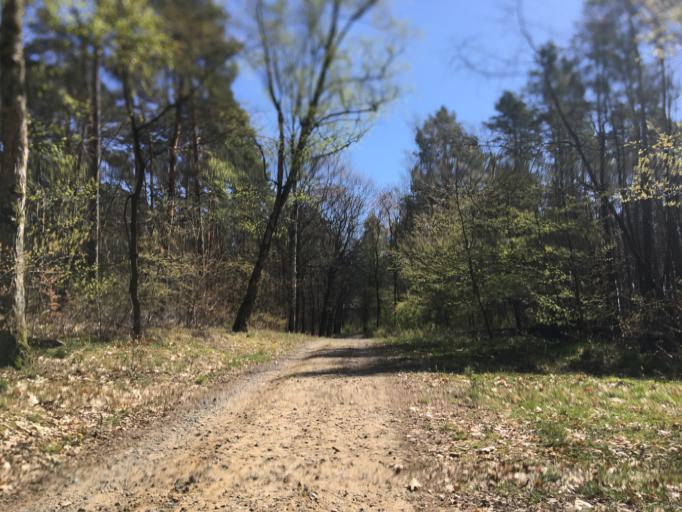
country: DE
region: Brandenburg
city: Bernau bei Berlin
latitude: 52.7003
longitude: 13.5361
